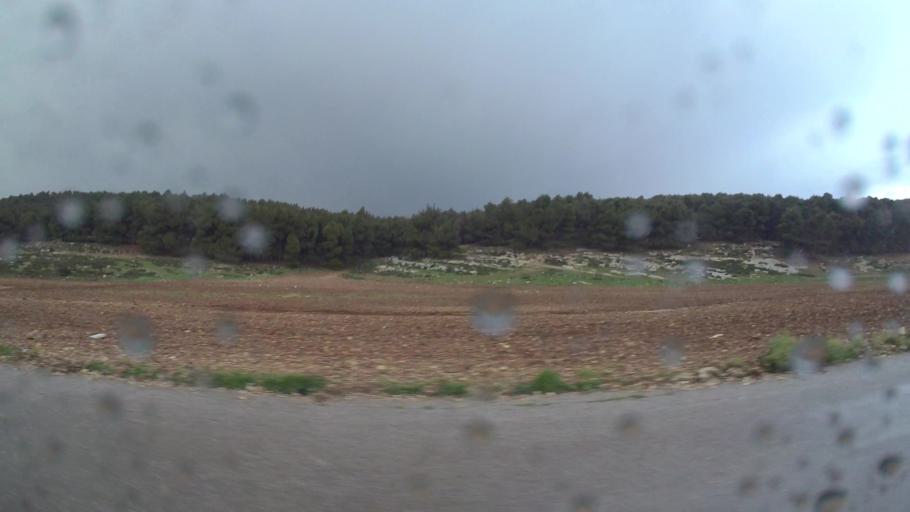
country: JO
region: Amman
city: Umm as Summaq
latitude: 31.8650
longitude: 35.8682
